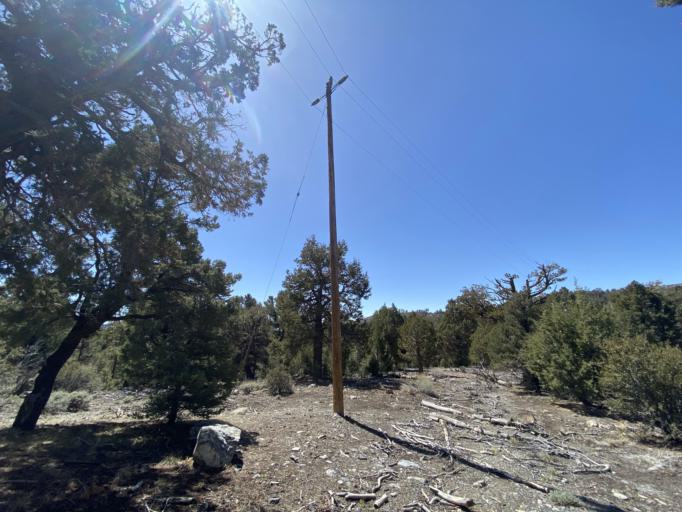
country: US
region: California
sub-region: San Bernardino County
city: Big Bear Lake
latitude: 34.3231
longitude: -116.9296
